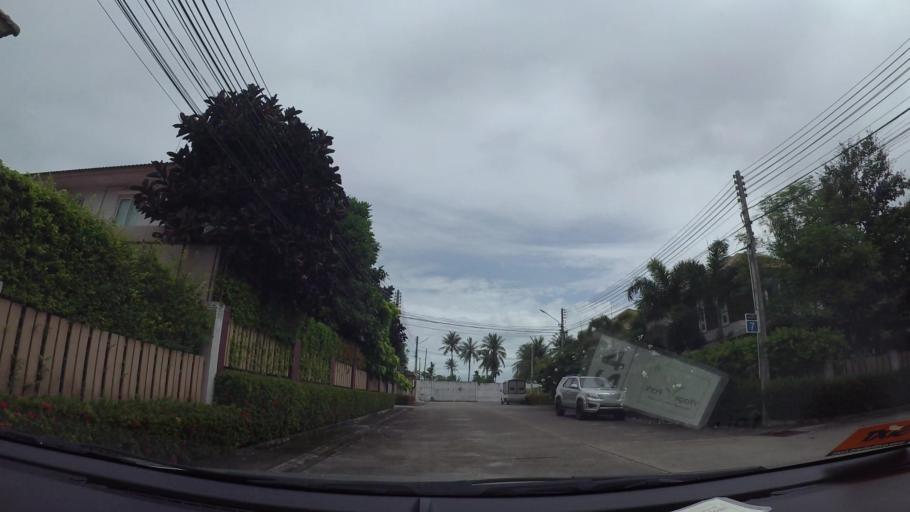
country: TH
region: Chon Buri
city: Si Racha
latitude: 13.1431
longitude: 100.9828
